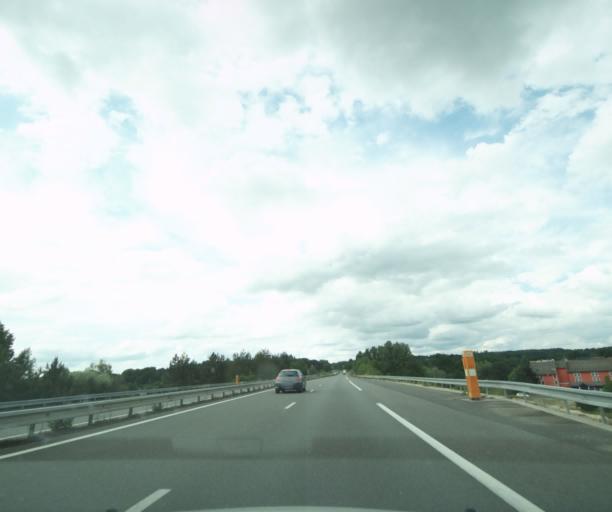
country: FR
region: Centre
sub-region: Departement du Cher
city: Vierzon
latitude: 47.2134
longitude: 2.1147
